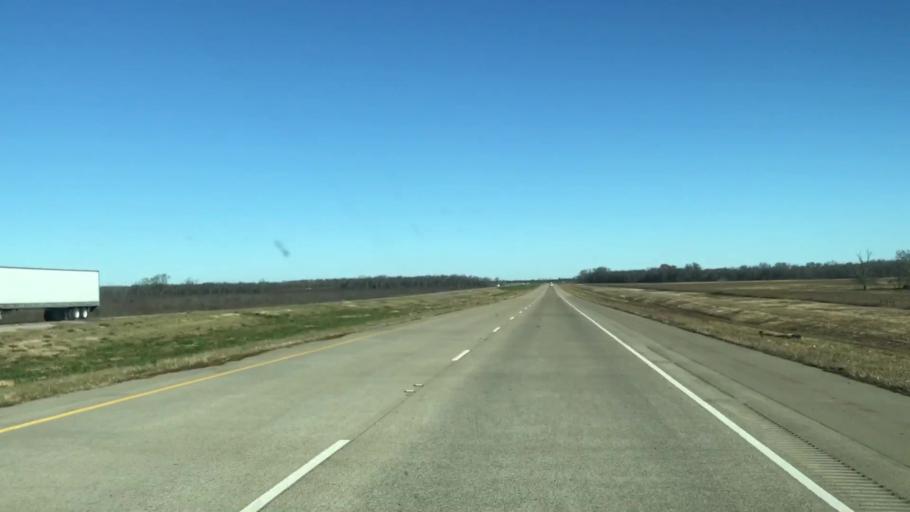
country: US
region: Louisiana
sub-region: Caddo Parish
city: Blanchard
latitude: 32.6317
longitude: -93.8373
